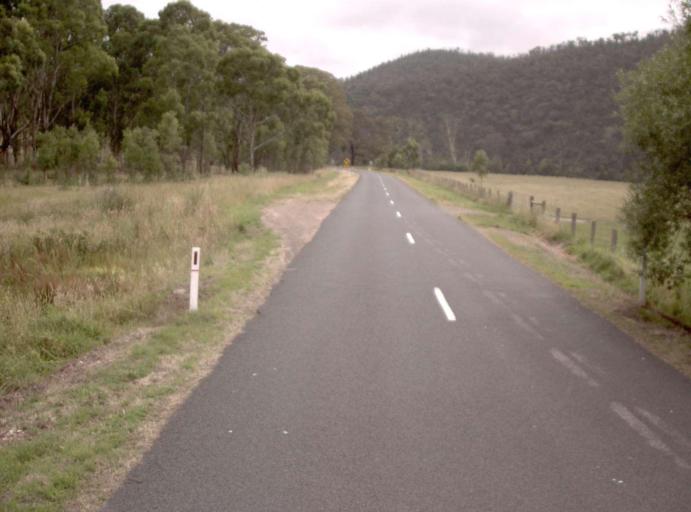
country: AU
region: Victoria
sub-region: Wellington
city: Heyfield
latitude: -37.7950
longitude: 146.6770
